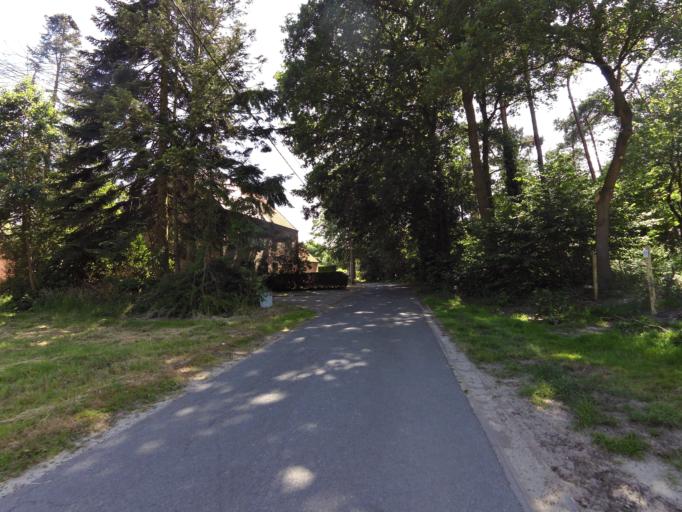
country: BE
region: Flanders
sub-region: Provincie West-Vlaanderen
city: Zedelgem
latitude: 51.1567
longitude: 3.1574
